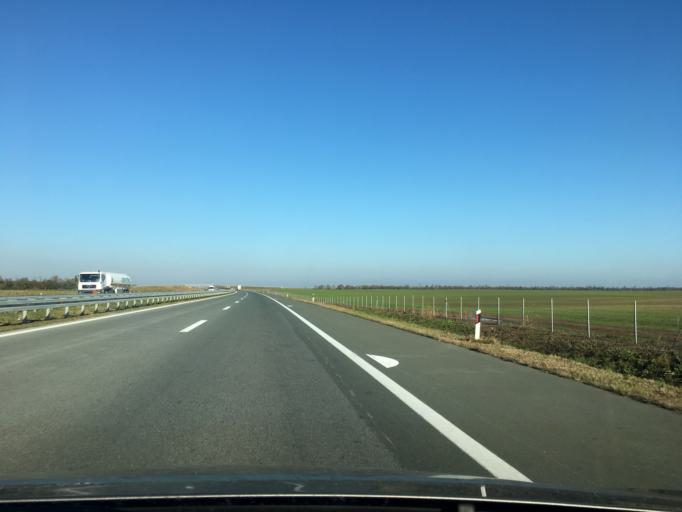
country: RS
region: Autonomna Pokrajina Vojvodina
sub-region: Severnobacki Okrug
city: Mali Igos
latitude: 45.6860
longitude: 19.7273
